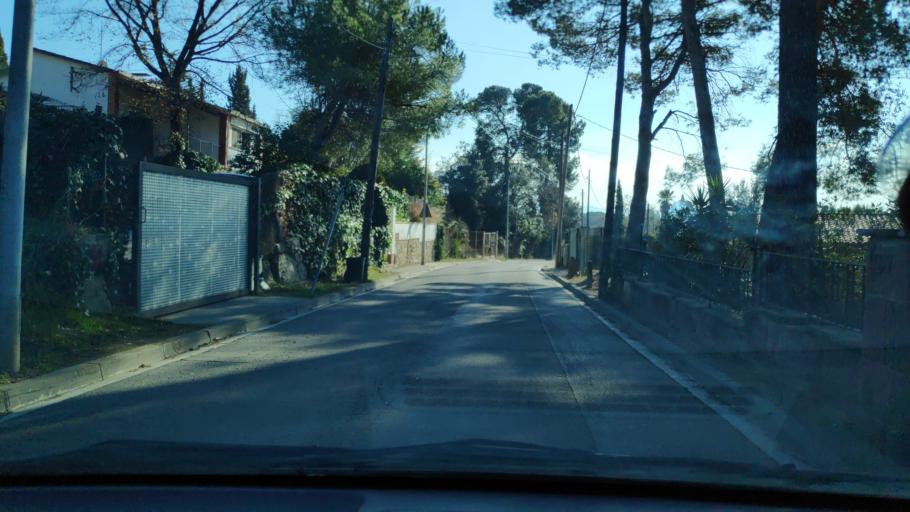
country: ES
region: Catalonia
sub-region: Provincia de Barcelona
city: Sant Cugat del Valles
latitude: 41.4990
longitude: 2.0806
